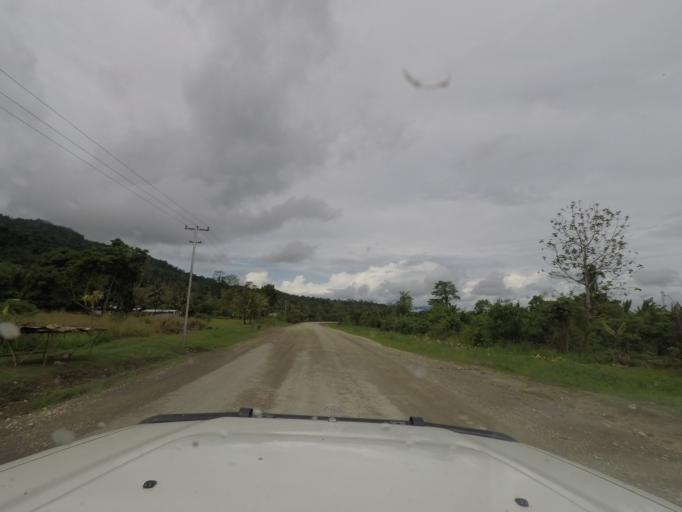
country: PG
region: Eastern Highlands
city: Goroka
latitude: -5.5930
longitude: 145.4621
